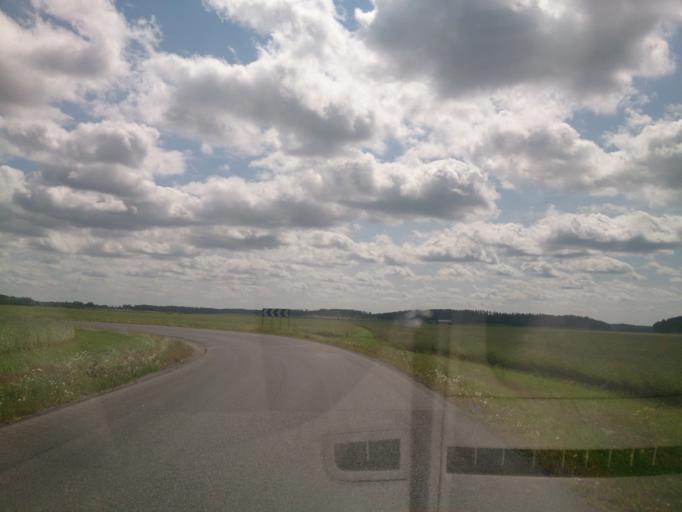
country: SE
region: OEstergoetland
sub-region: Norrkopings Kommun
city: Krokek
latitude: 58.5212
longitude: 16.4910
